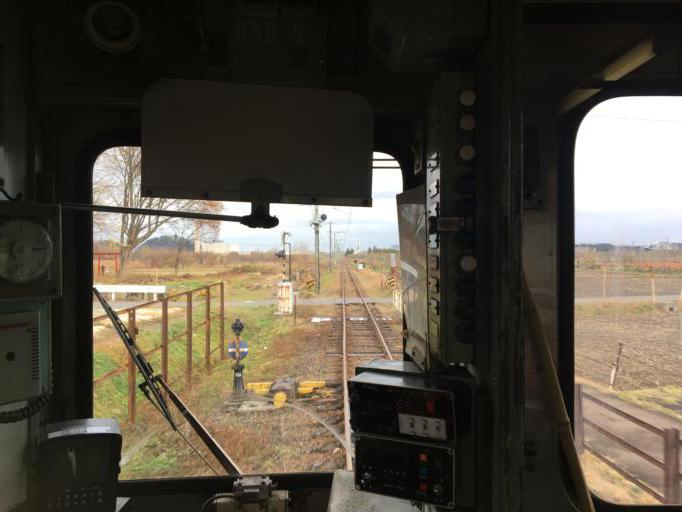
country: JP
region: Aomori
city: Hirosaki
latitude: 40.5365
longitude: 140.5525
